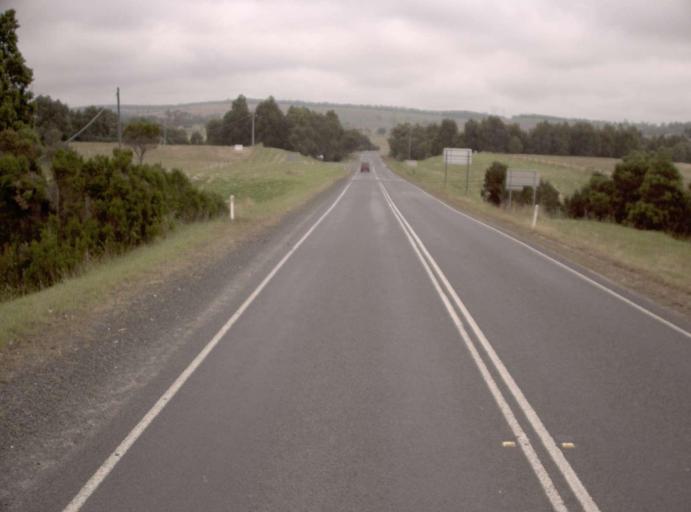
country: AU
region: Victoria
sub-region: Latrobe
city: Traralgon
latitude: -38.2492
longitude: 146.5465
